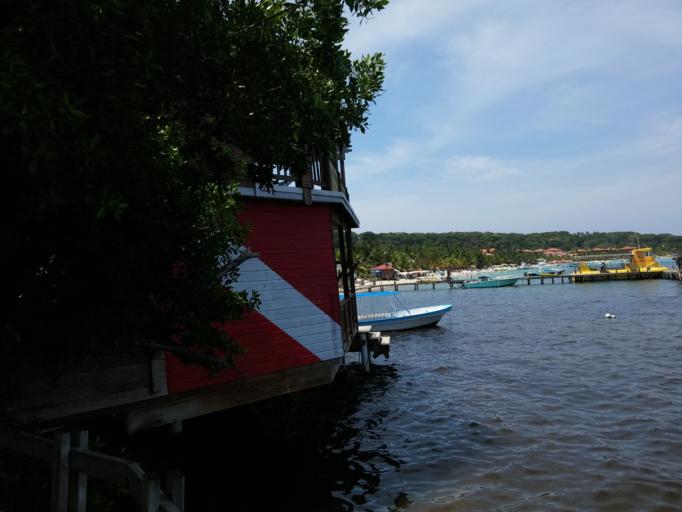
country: HN
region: Bay Islands
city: Sandy Bay
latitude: 16.2794
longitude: -86.5999
